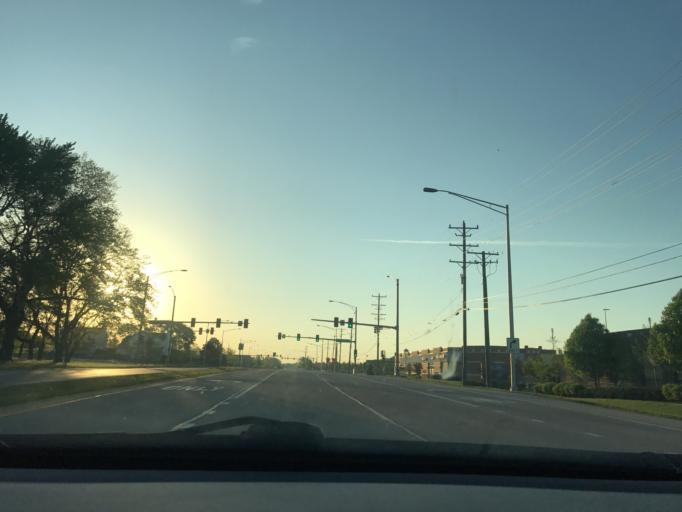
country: US
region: Illinois
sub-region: Kane County
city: South Elgin
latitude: 42.0069
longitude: -88.3402
